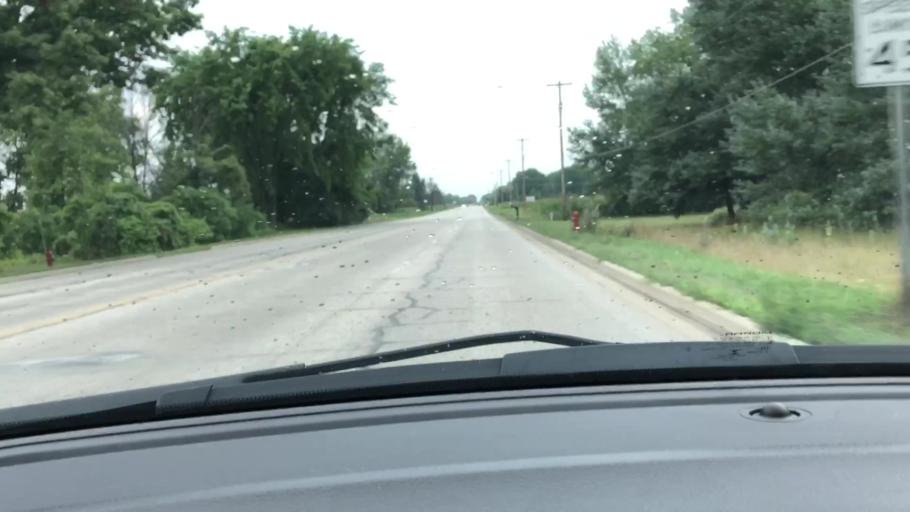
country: US
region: Michigan
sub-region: Saginaw County
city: Carrollton
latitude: 43.4805
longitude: -84.0047
